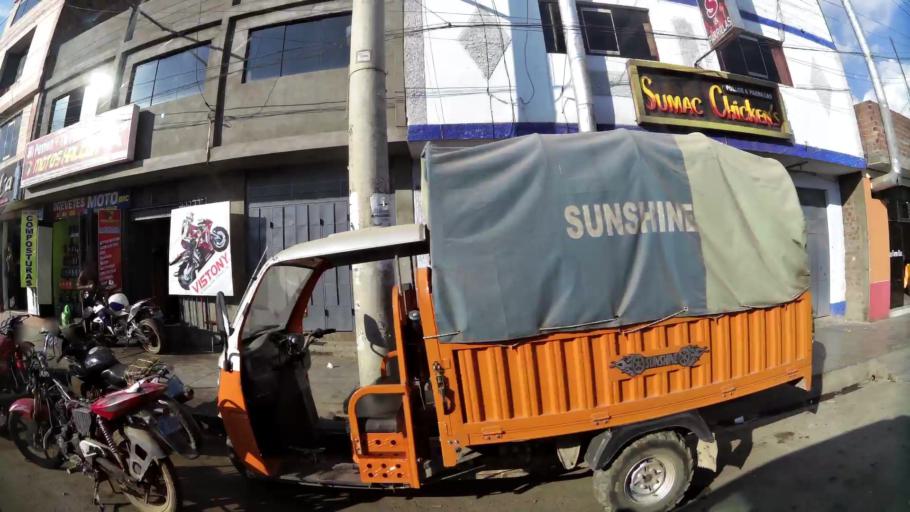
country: PE
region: Junin
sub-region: Provincia de Huancayo
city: El Tambo
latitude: -12.0495
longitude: -75.2155
